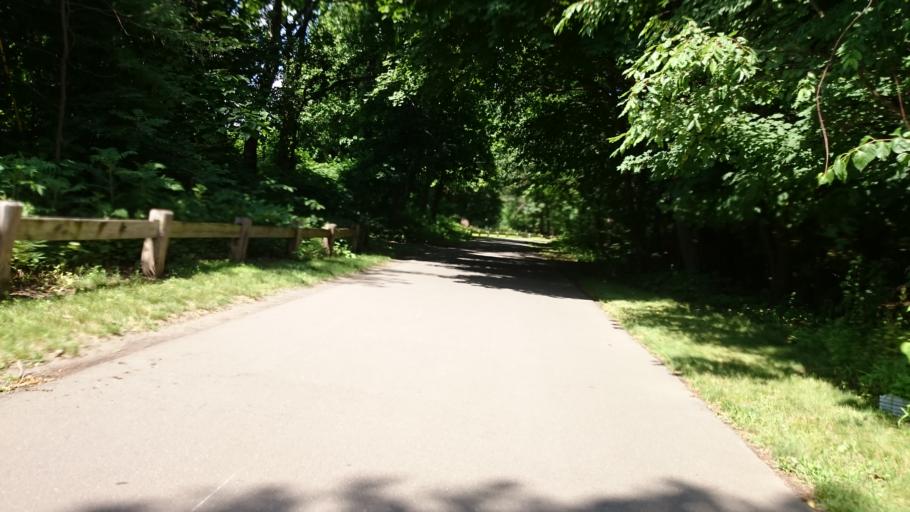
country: US
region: Connecticut
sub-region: New Haven County
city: New Haven
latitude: 41.3475
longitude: -72.9305
